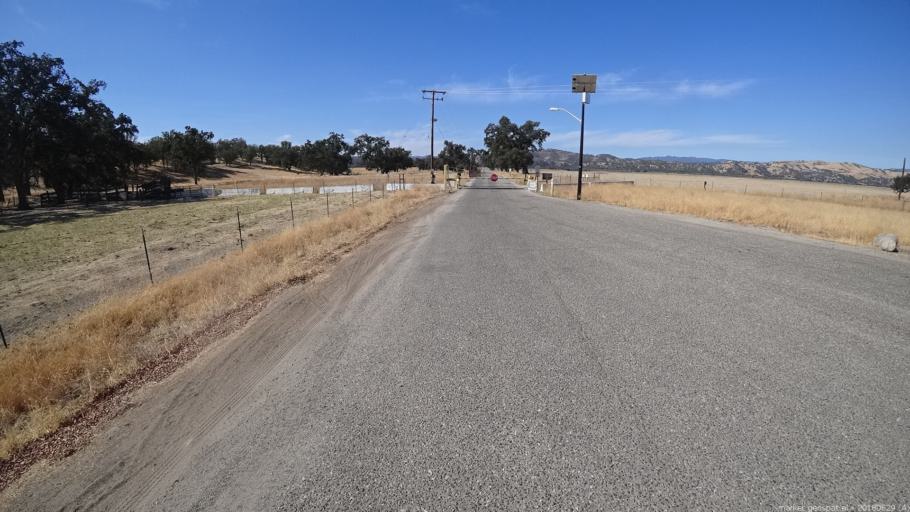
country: US
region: California
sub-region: Monterey County
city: King City
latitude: 35.9369
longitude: -121.1240
